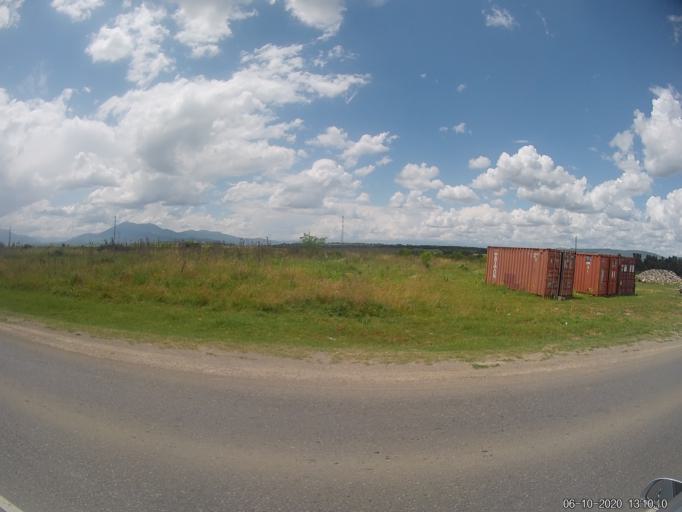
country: XK
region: Prizren
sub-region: Komuna e Therandes
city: Gjinoc
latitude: 42.3114
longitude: 20.8006
